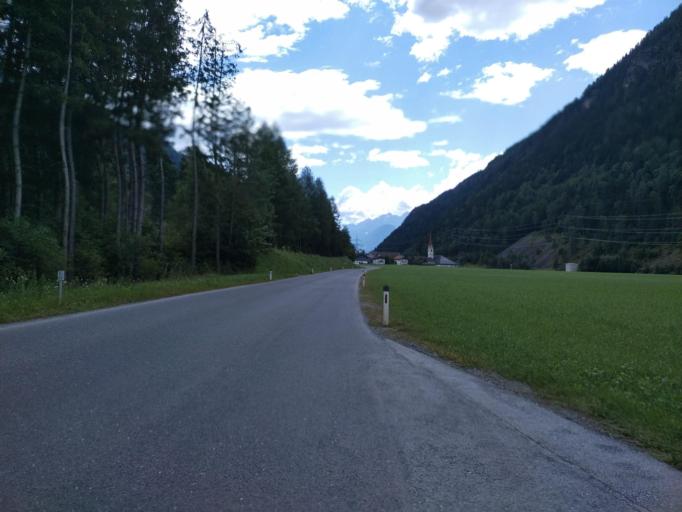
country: AT
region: Tyrol
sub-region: Politischer Bezirk Lienz
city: Schlaiten
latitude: 46.9061
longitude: 12.6219
